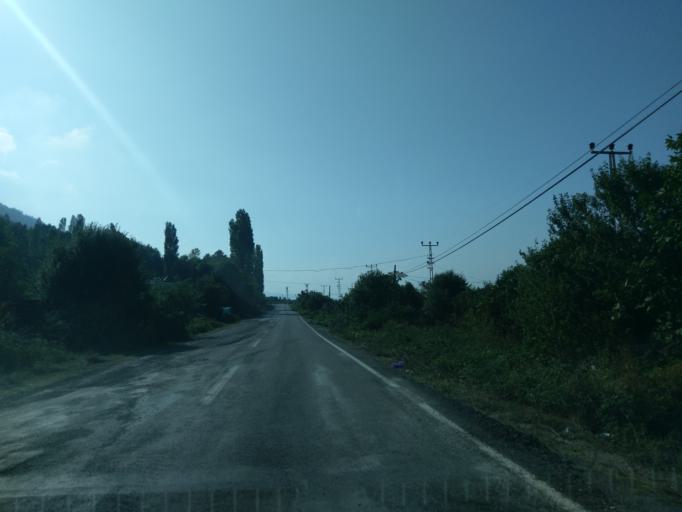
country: TR
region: Sinop
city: Ayancik
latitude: 41.9411
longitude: 34.6565
